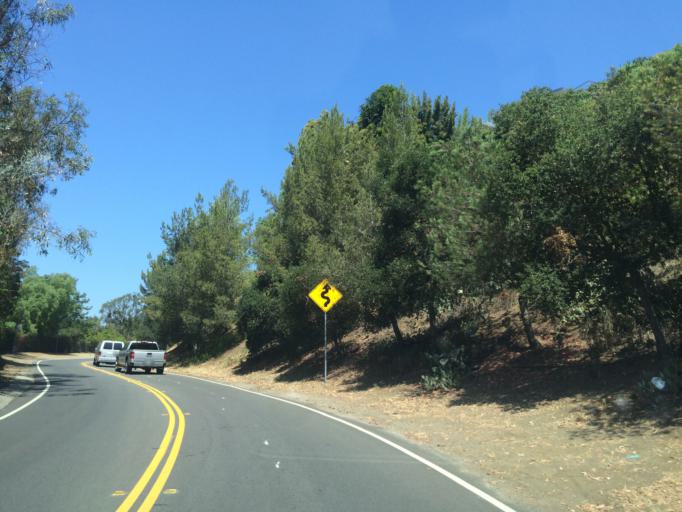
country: US
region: California
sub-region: Los Angeles County
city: Universal City
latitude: 34.1176
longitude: -118.3449
